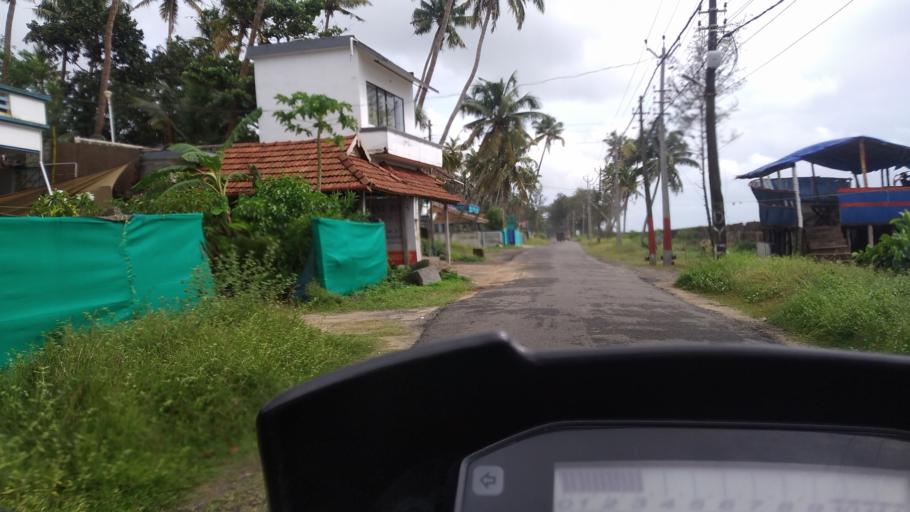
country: IN
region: Kerala
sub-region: Thrissur District
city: Kodungallur
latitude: 10.1561
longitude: 76.1735
